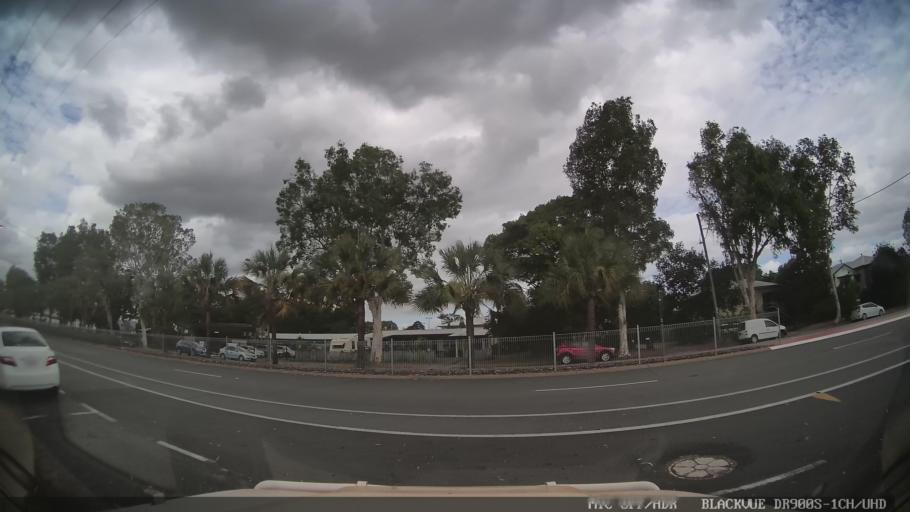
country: AU
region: Queensland
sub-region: Cairns
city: Cairns
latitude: -16.9236
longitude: 145.7504
